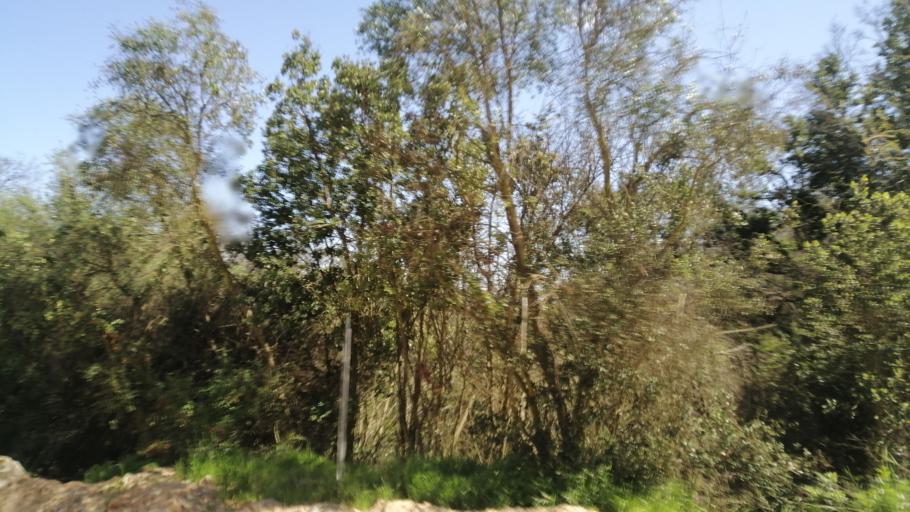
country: CL
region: Valparaiso
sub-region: Provincia de Marga Marga
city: Limache
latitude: -33.2057
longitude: -71.2539
